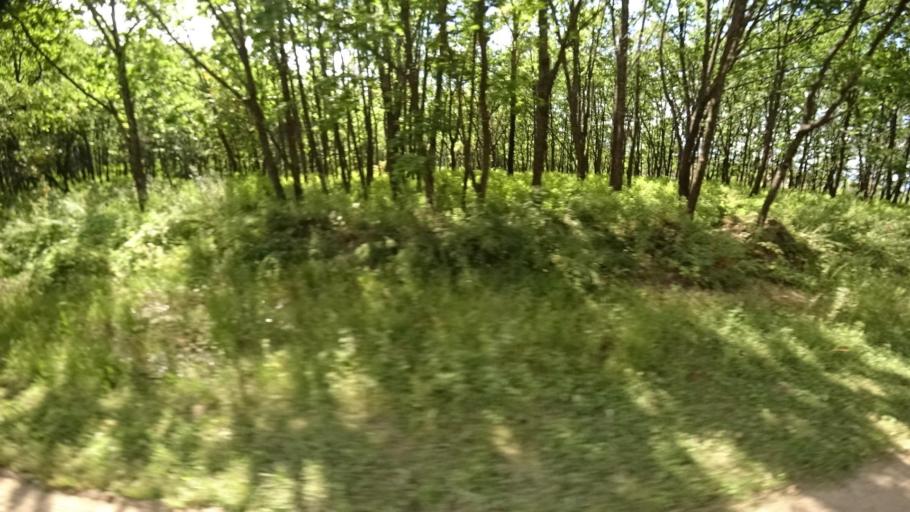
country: RU
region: Primorskiy
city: Yakovlevka
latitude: 44.4098
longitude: 133.5693
